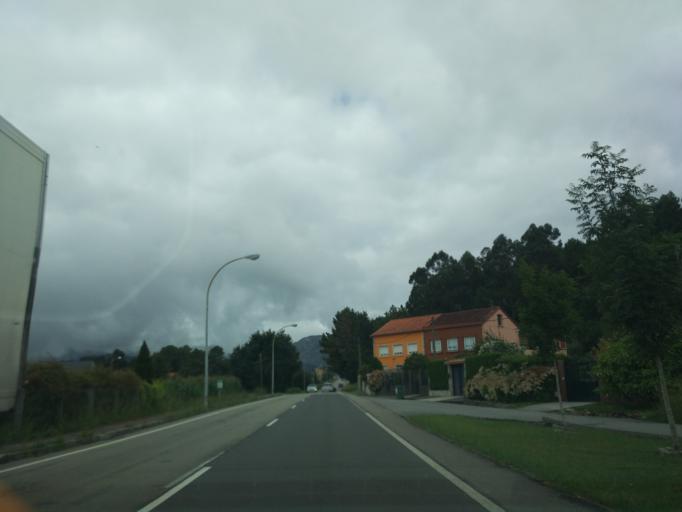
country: ES
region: Galicia
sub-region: Provincia da Coruna
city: Boiro
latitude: 42.6428
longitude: -8.8684
